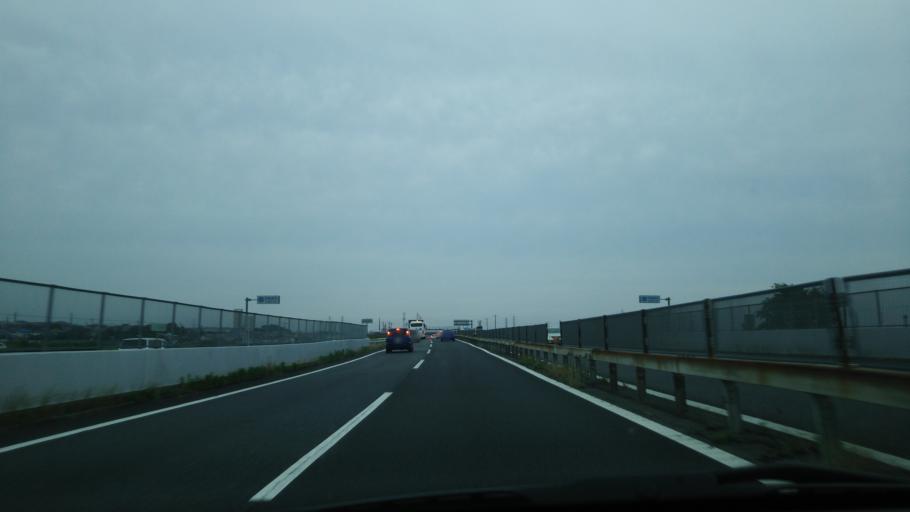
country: JP
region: Kanagawa
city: Isehara
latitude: 35.3803
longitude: 139.3291
